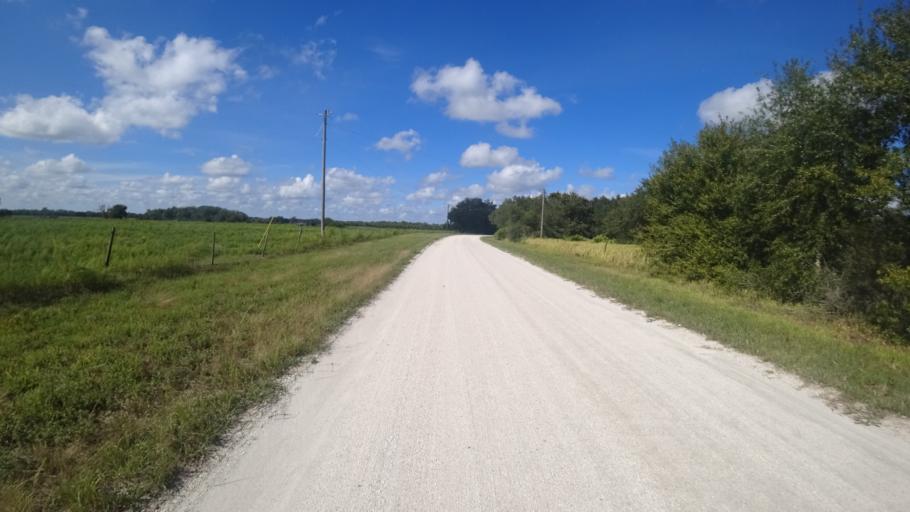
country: US
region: Florida
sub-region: DeSoto County
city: Arcadia
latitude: 27.3555
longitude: -82.1258
